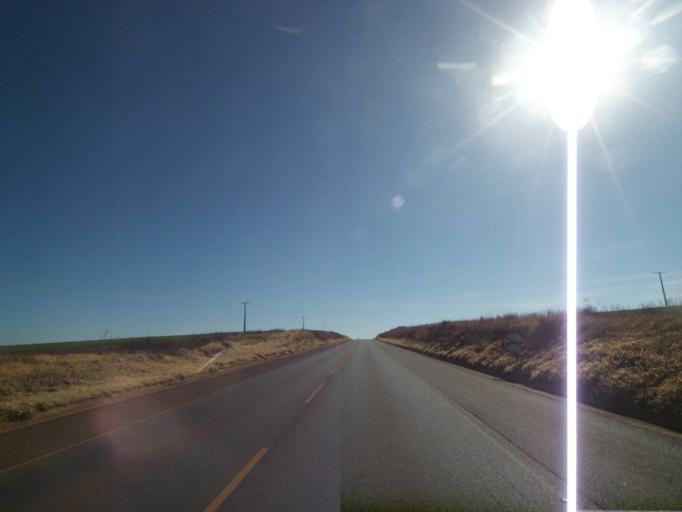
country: BR
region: Parana
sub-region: Tibagi
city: Tibagi
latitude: -24.4513
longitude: -50.4236
